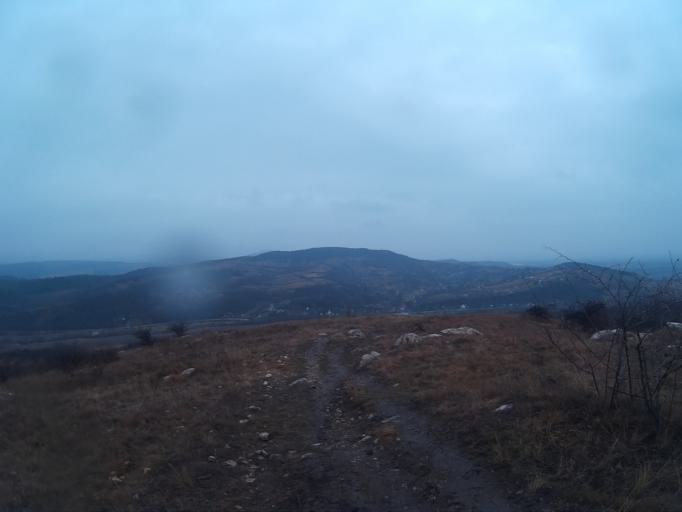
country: HU
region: Komarom-Esztergom
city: Tokod
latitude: 47.7141
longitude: 18.6375
